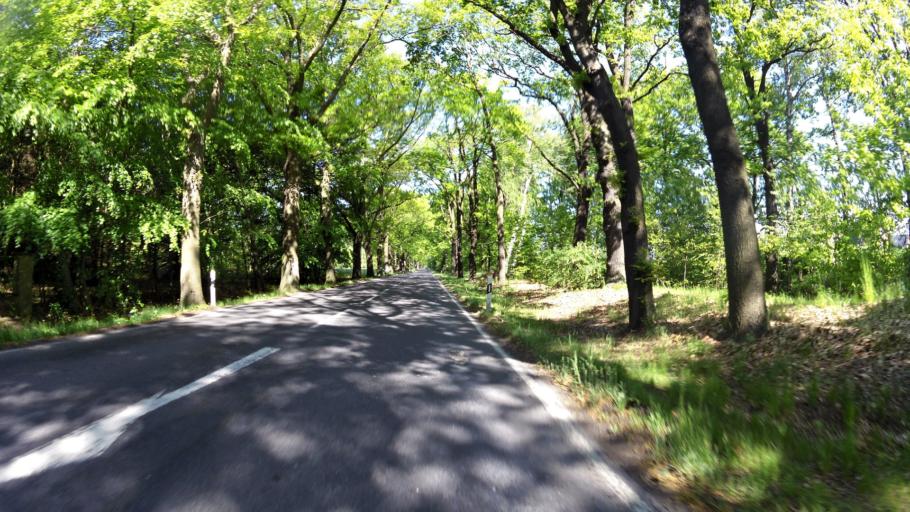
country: DE
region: Saxony
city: Bernsdorf
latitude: 51.3807
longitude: 14.0563
